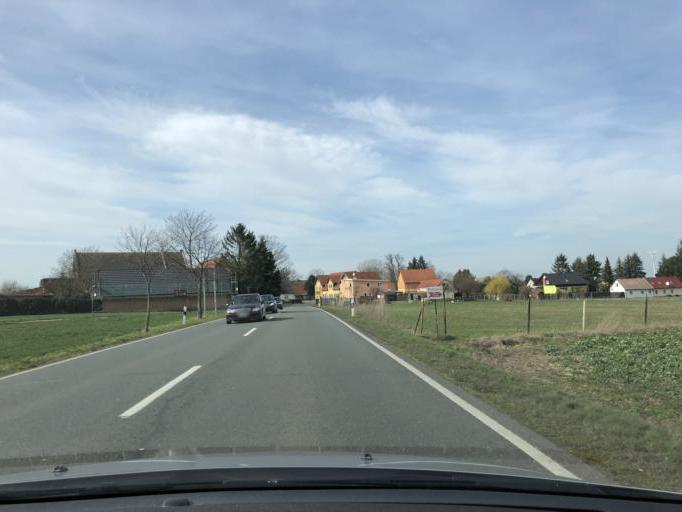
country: DE
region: Saxony-Anhalt
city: Osterfeld
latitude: 51.0849
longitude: 11.9694
